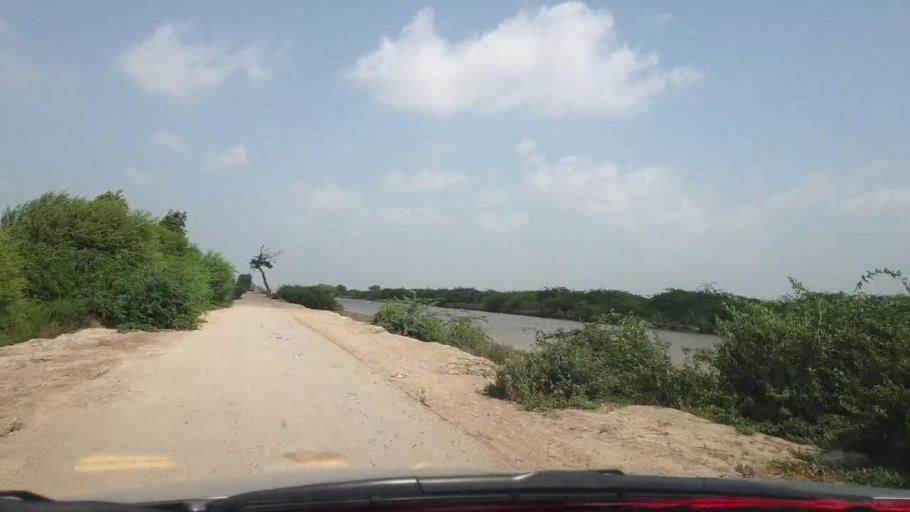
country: PK
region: Sindh
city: Talhar
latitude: 24.8915
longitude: 68.8352
